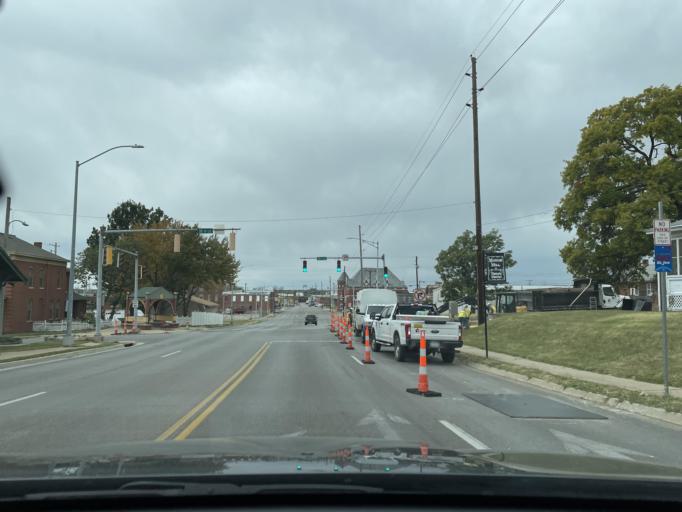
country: US
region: Missouri
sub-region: Buchanan County
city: Saint Joseph
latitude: 39.7625
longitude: -94.8489
